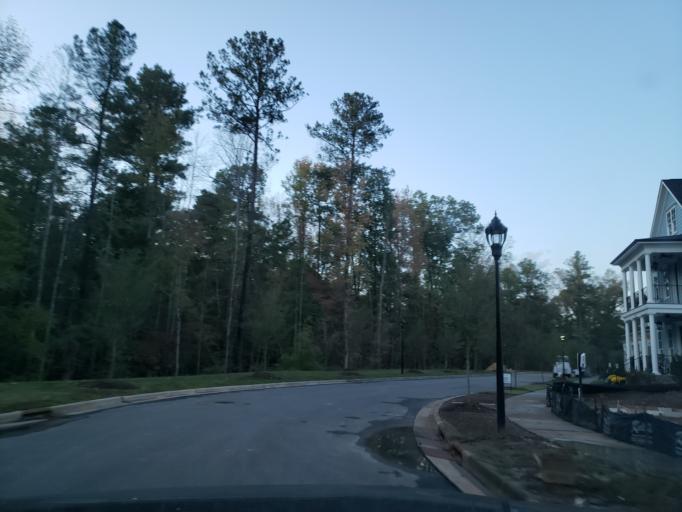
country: US
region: North Carolina
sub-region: Orange County
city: Chapel Hill
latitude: 35.8801
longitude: -78.9584
